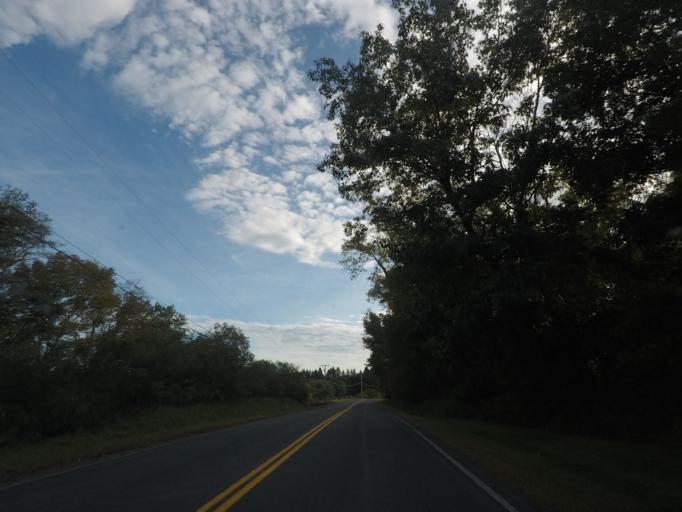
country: US
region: New York
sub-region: Rensselaer County
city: West Sand Lake
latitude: 42.6212
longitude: -73.6370
